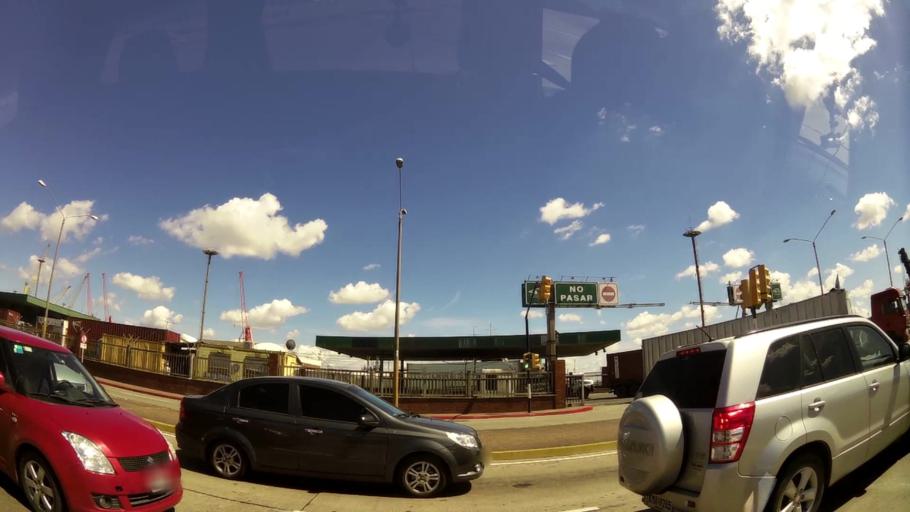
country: UY
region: Montevideo
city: Montevideo
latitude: -34.9010
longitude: -56.1999
